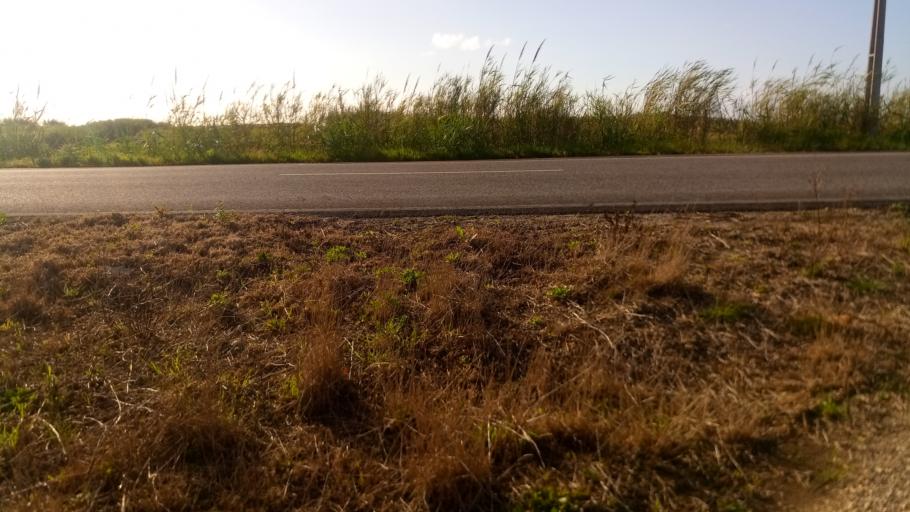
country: PT
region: Leiria
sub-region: Caldas da Rainha
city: Caldas da Rainha
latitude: 39.4616
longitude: -9.1976
